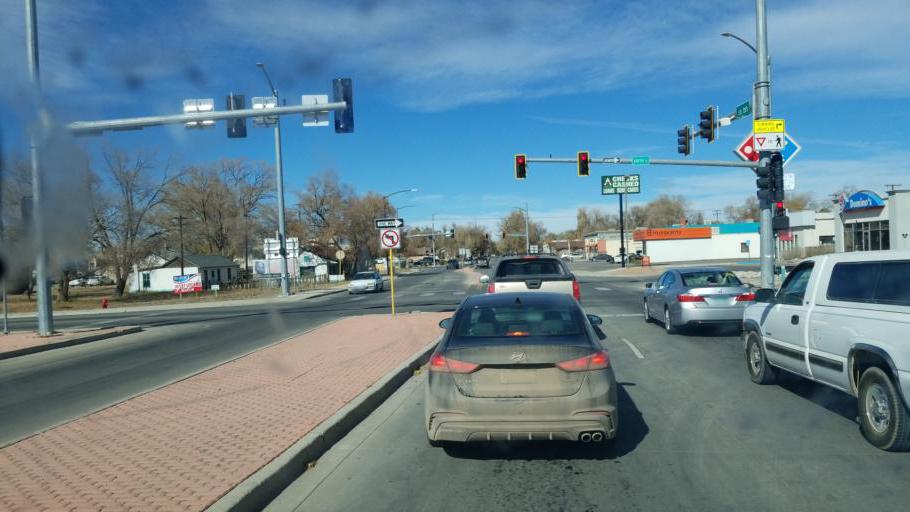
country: US
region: Colorado
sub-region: Alamosa County
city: Alamosa
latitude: 37.4671
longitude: -105.8743
